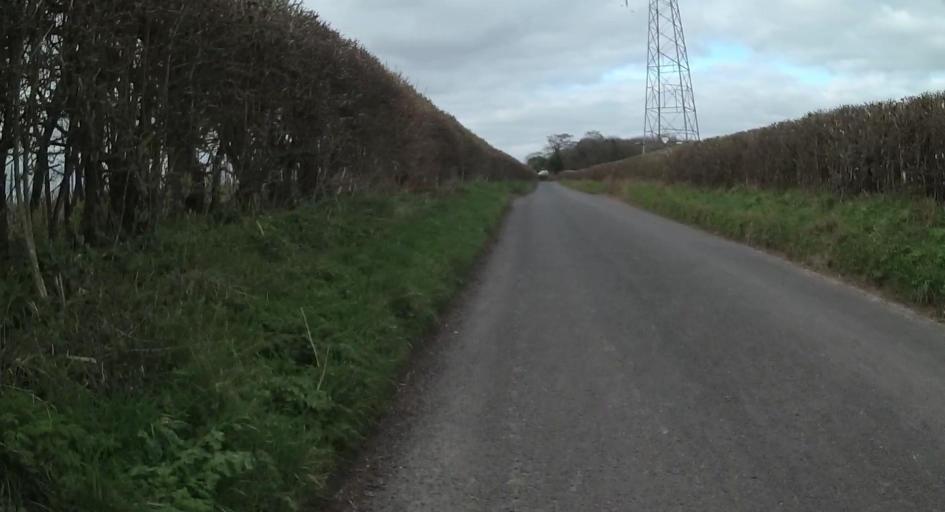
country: GB
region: England
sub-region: Hampshire
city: Abbotts Ann
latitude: 51.1538
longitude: -1.4888
